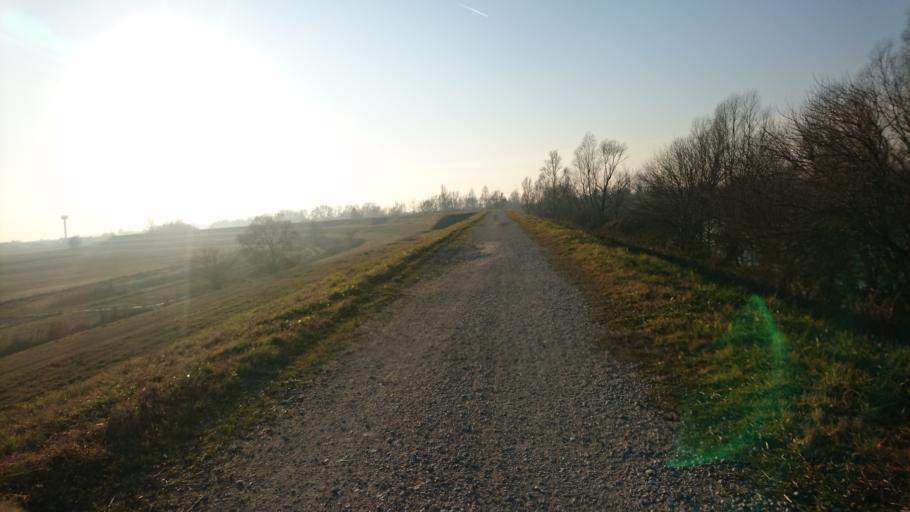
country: IT
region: Veneto
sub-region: Provincia di Padova
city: Boara Pisani
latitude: 45.1213
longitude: 11.8103
